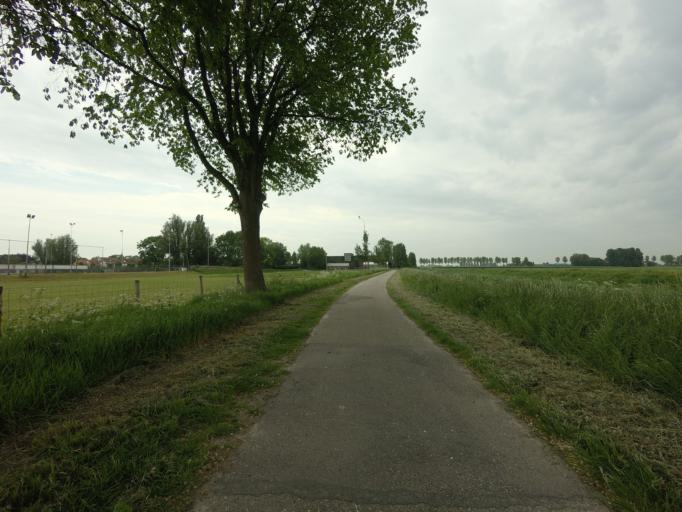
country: NL
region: South Holland
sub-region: Gemeente Spijkenisse
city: Spijkenisse
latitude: 51.7955
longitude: 4.3091
